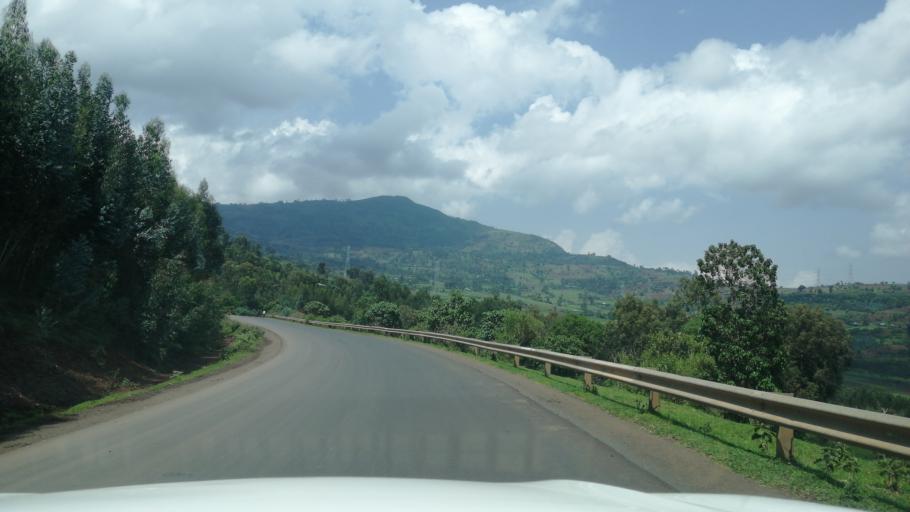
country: ET
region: Oromiya
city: Gedo
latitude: 8.9748
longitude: 37.5850
